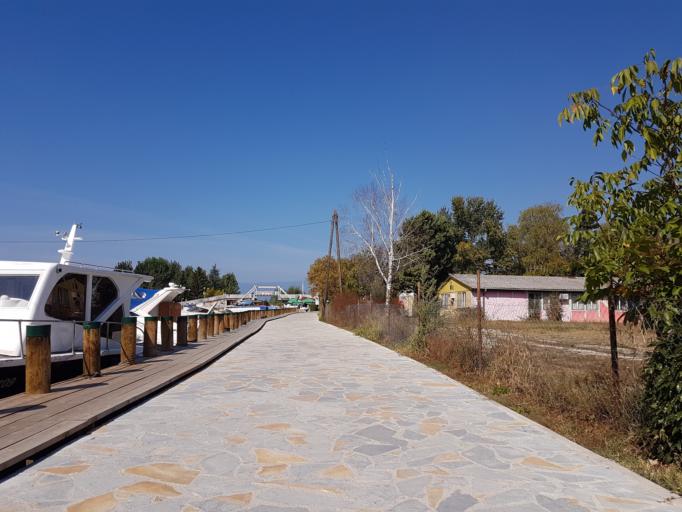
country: MK
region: Ohrid
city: Ohrid
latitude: 41.1036
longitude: 20.8096
